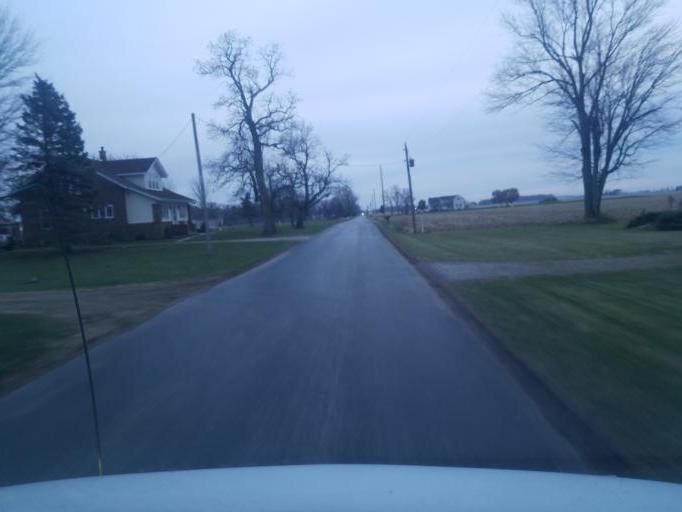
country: US
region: Indiana
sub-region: Adams County
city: Decatur
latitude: 40.7855
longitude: -85.0148
